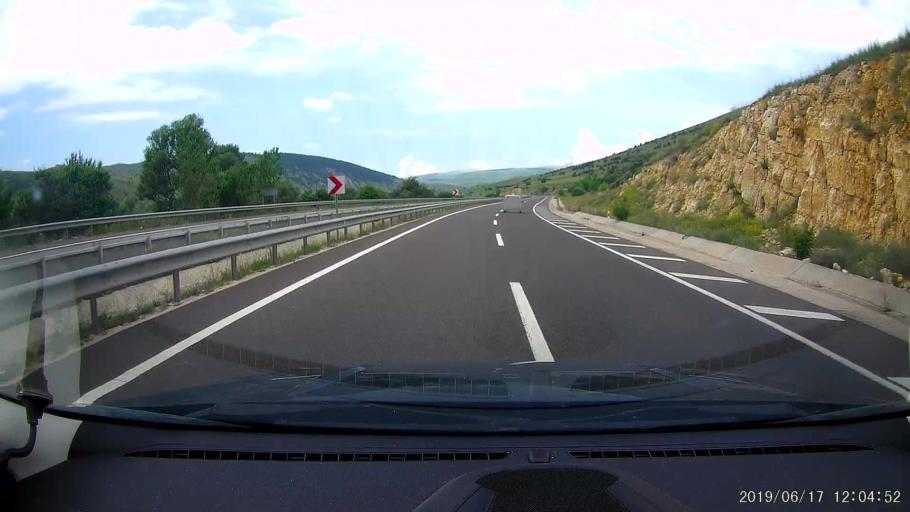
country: TR
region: Cankiri
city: Cerkes
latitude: 40.8267
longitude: 32.7910
